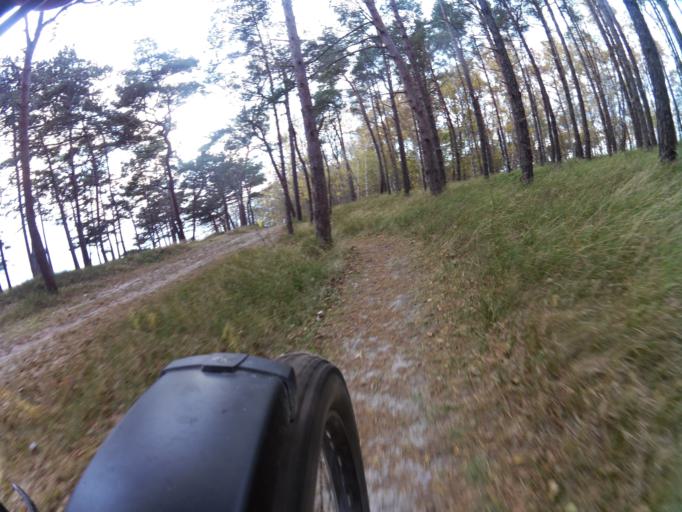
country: PL
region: Pomeranian Voivodeship
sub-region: Powiat pucki
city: Jastarnia
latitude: 54.7210
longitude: 18.6222
